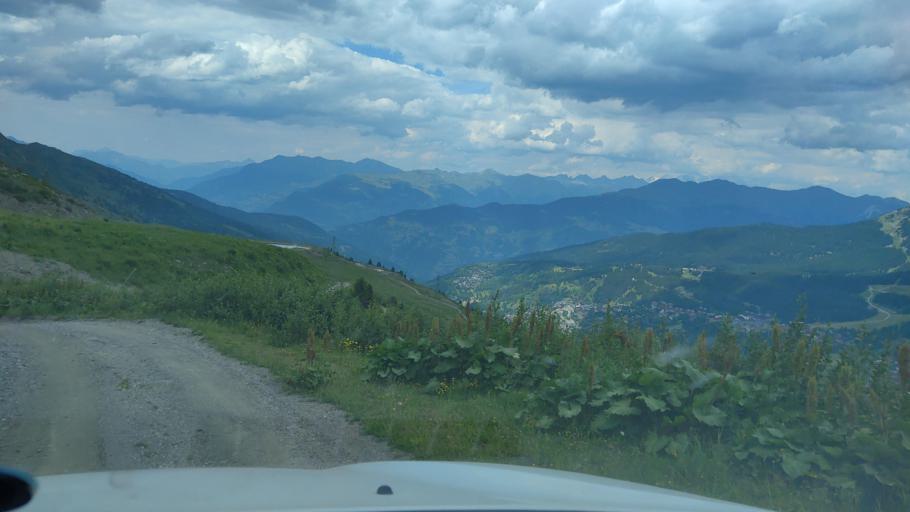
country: FR
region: Rhone-Alpes
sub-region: Departement de la Savoie
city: Meribel
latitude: 45.3732
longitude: 6.5572
